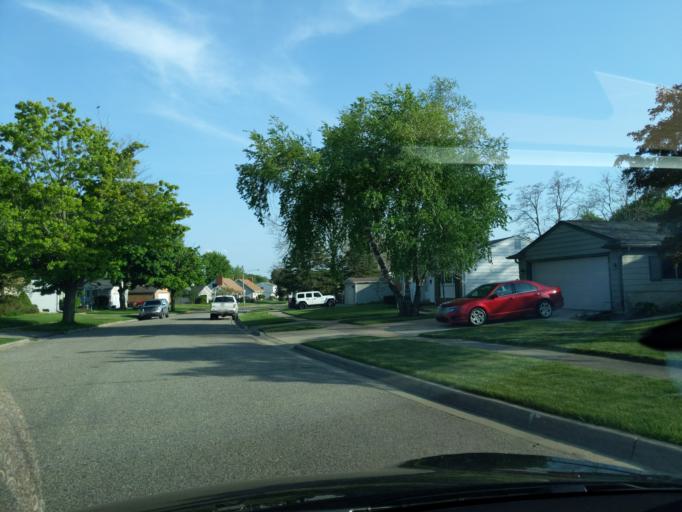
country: US
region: Michigan
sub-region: Ingham County
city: East Lansing
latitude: 42.7535
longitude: -84.5161
